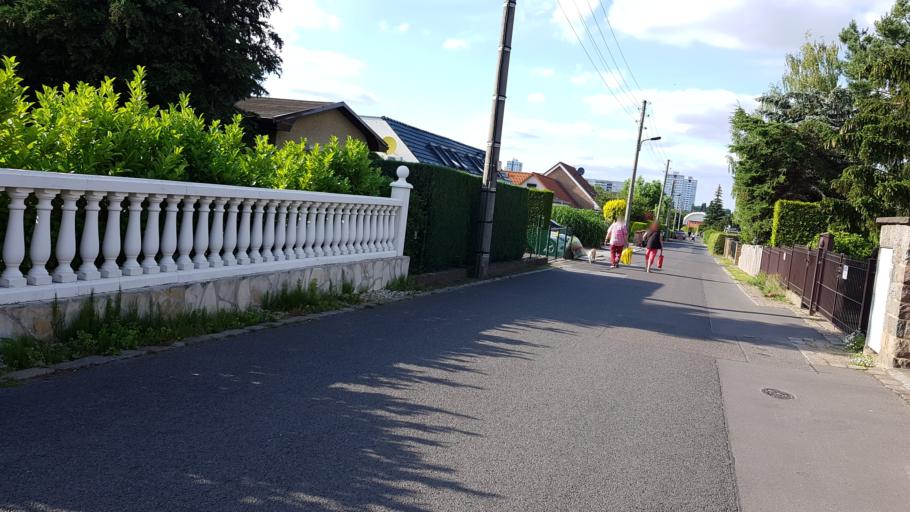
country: DE
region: Berlin
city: Marzahn
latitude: 52.5315
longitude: 13.5669
